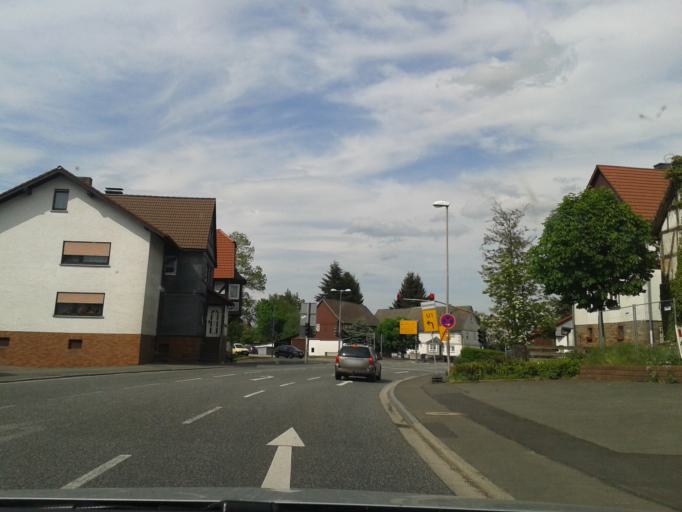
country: DE
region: Hesse
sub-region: Regierungsbezirk Giessen
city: Munchhausen
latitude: 50.9611
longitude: 8.7162
